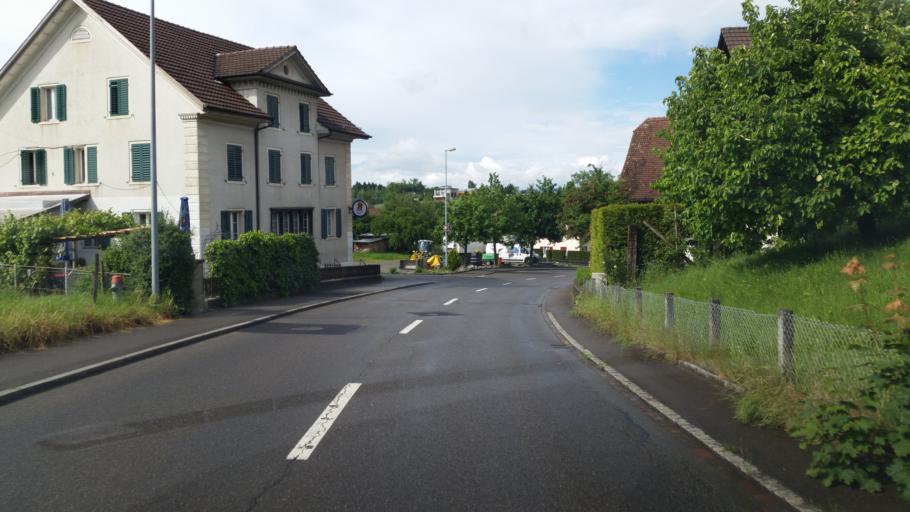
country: CH
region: Aargau
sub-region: Bezirk Bremgarten
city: Sarmenstorf
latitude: 47.3250
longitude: 8.2681
